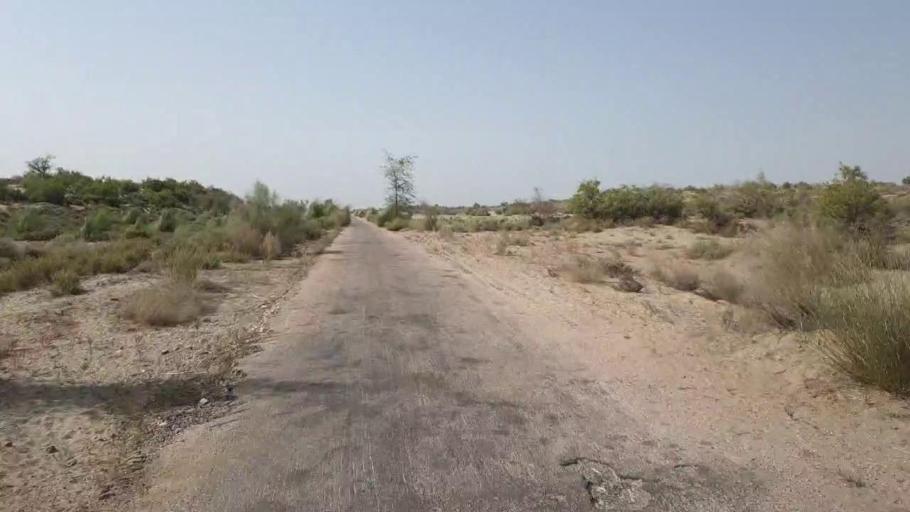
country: PK
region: Sindh
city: Jam Sahib
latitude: 26.5692
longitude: 68.9224
